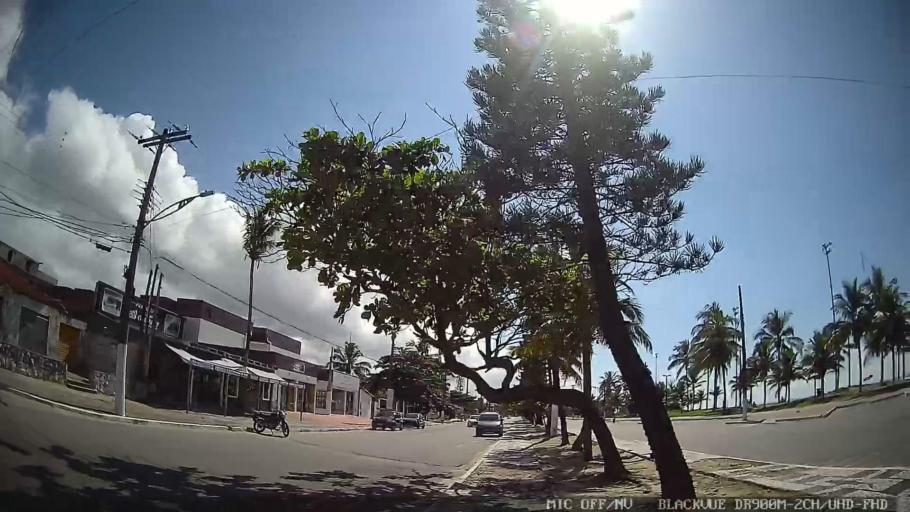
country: BR
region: Sao Paulo
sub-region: Peruibe
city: Peruibe
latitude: -24.3236
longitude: -46.9944
